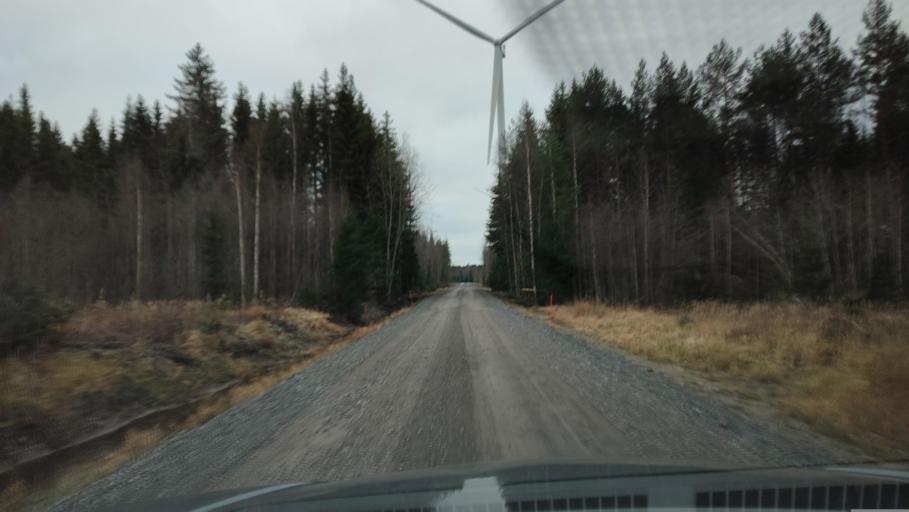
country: FI
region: Southern Ostrobothnia
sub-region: Suupohja
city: Karijoki
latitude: 62.2121
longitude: 21.6016
